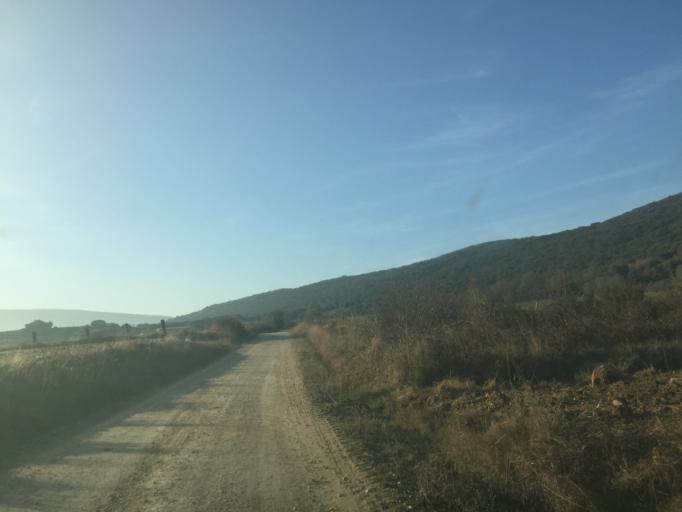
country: ES
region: Castille and Leon
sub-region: Provincia de Burgos
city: Medina de Pomar
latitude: 42.9299
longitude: -3.5935
